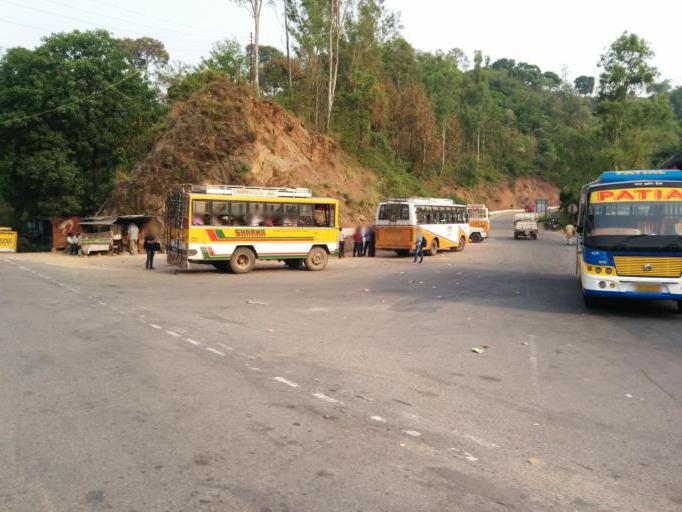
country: IN
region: Himachal Pradesh
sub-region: Kangra
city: Kotla
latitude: 32.2284
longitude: 76.0812
